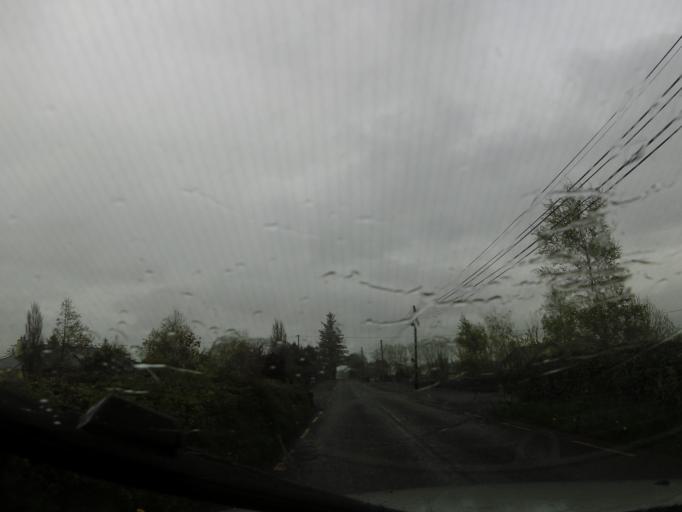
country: IE
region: Connaught
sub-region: Maigh Eo
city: Ballinrobe
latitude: 53.5560
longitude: -9.2533
